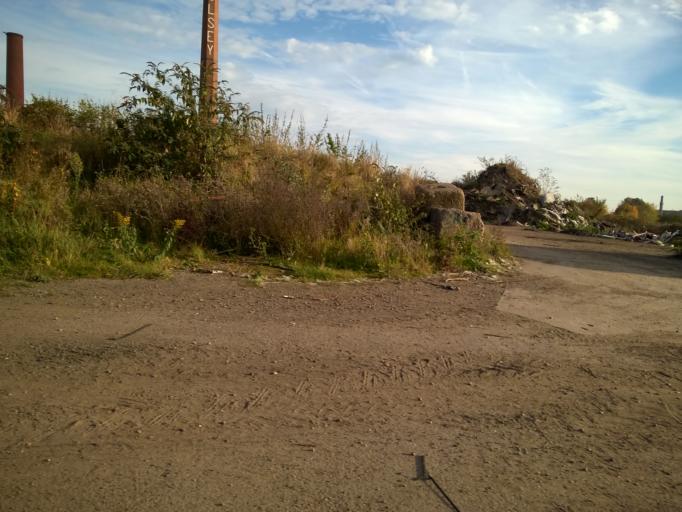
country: GB
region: England
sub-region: City of Leicester
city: Leicester
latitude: 52.6523
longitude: -1.1321
